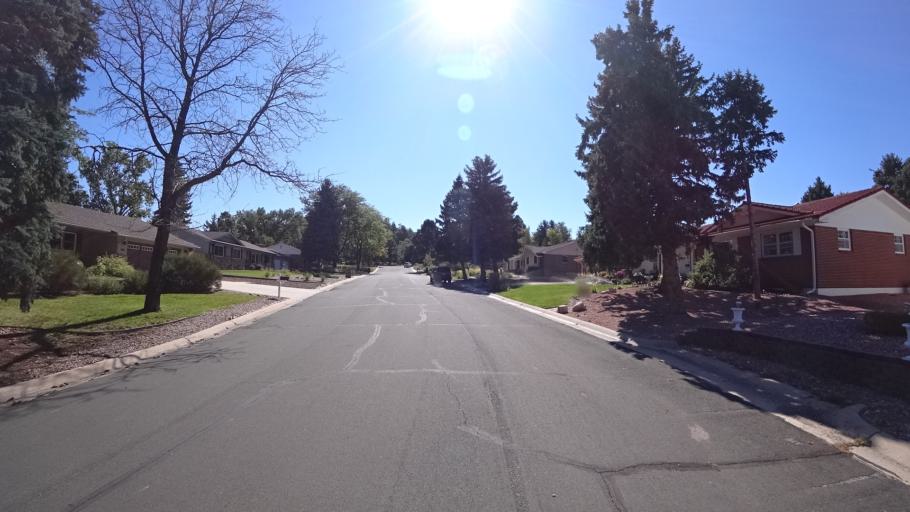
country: US
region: Colorado
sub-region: El Paso County
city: Colorado Springs
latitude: 38.8751
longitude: -104.7813
